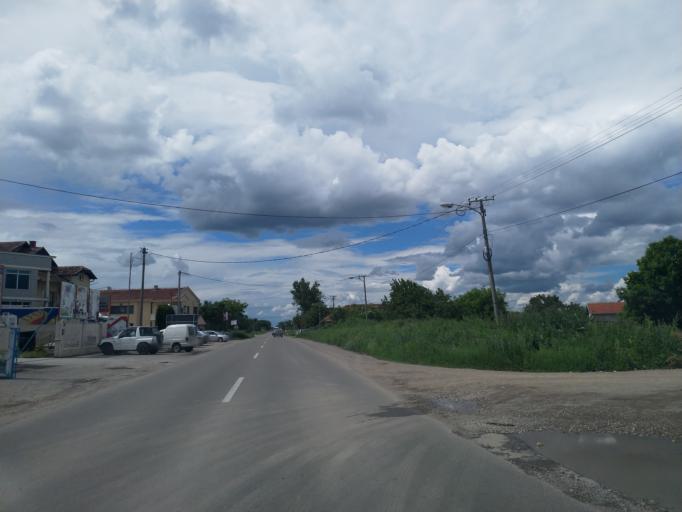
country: RS
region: Central Serbia
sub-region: Pomoravski Okrug
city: Paracin
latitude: 43.8732
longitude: 21.3984
